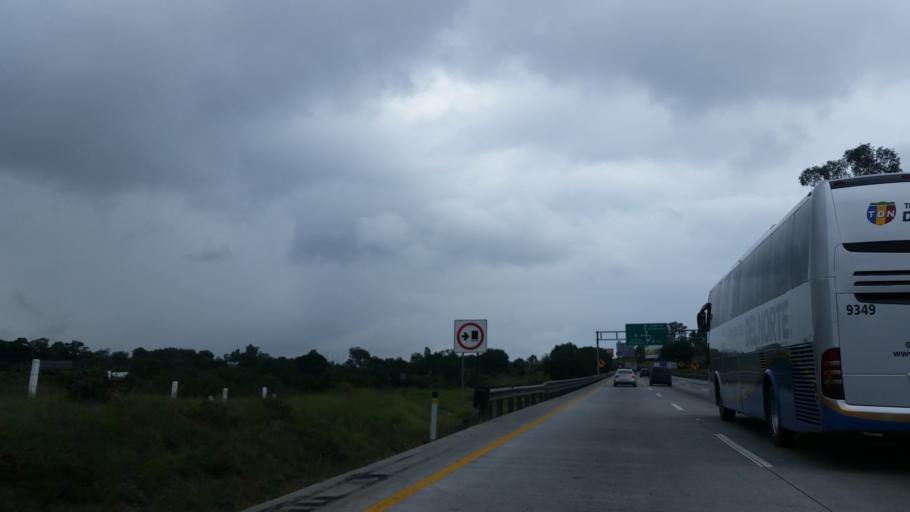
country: MX
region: Hidalgo
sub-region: Tepeji del Rio de Ocampo
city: Santiago Tlautla
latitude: 19.9755
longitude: -99.4360
